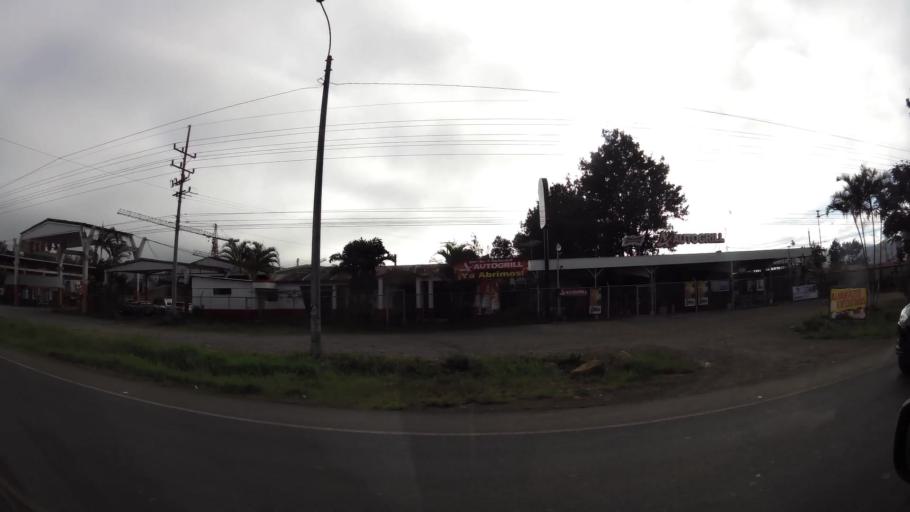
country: CR
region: Cartago
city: Cartago
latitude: 9.8578
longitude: -83.9473
